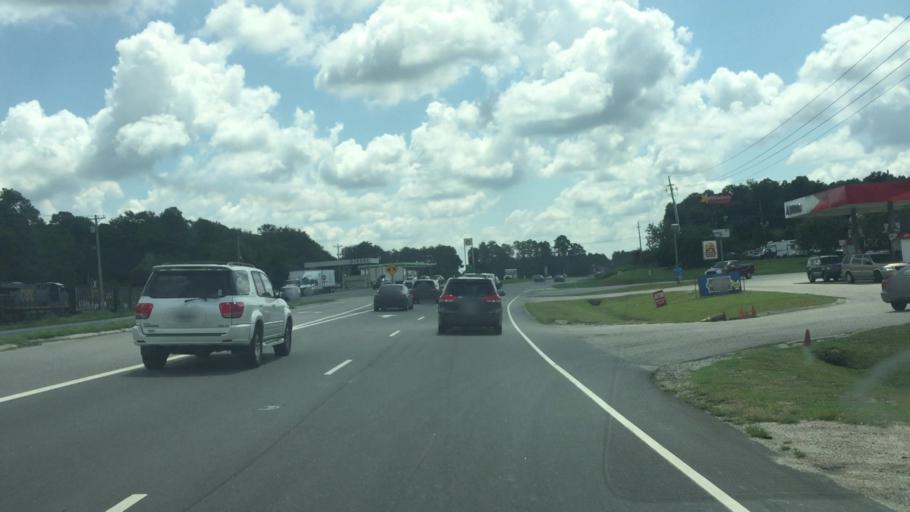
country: US
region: North Carolina
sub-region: Scotland County
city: Laurel Hill
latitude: 34.8075
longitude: -79.5455
